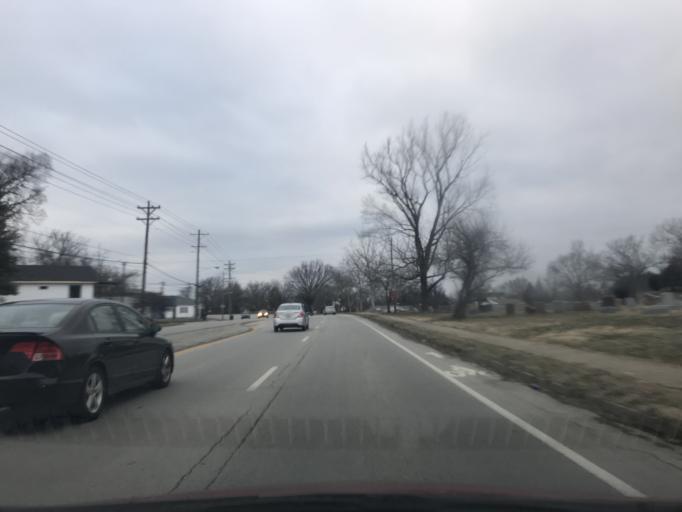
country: US
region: Kentucky
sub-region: Jefferson County
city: Audubon Park
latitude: 38.2214
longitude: -85.7290
